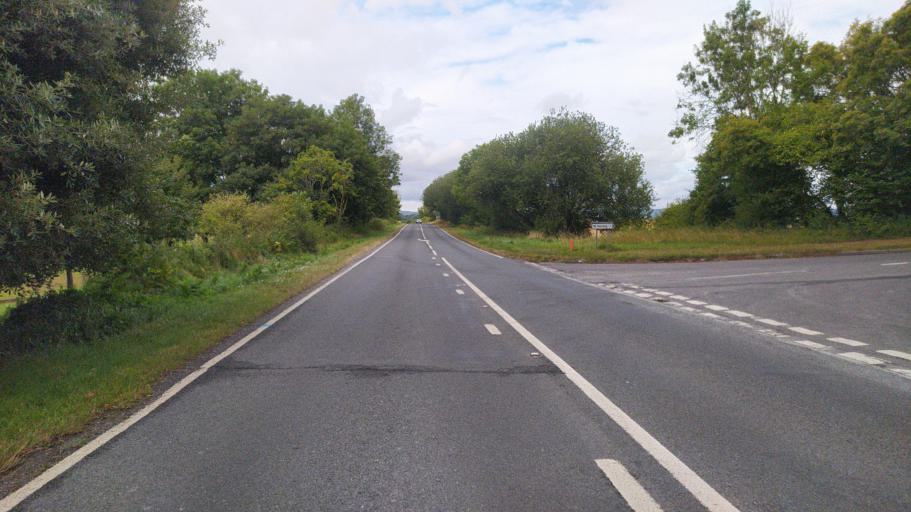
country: GB
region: England
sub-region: Hampshire
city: Petersfield
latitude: 50.9722
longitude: -0.8956
